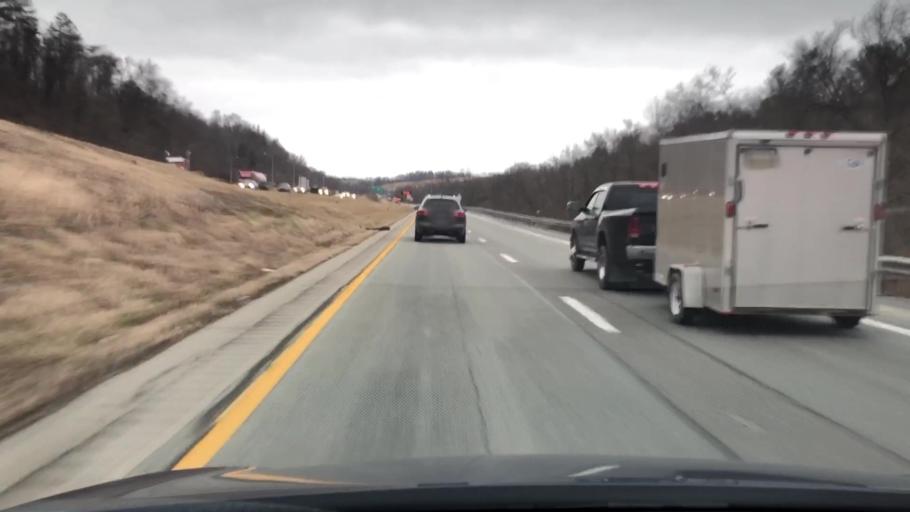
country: US
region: Pennsylvania
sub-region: Washington County
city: East Washington
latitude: 40.1193
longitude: -80.2043
